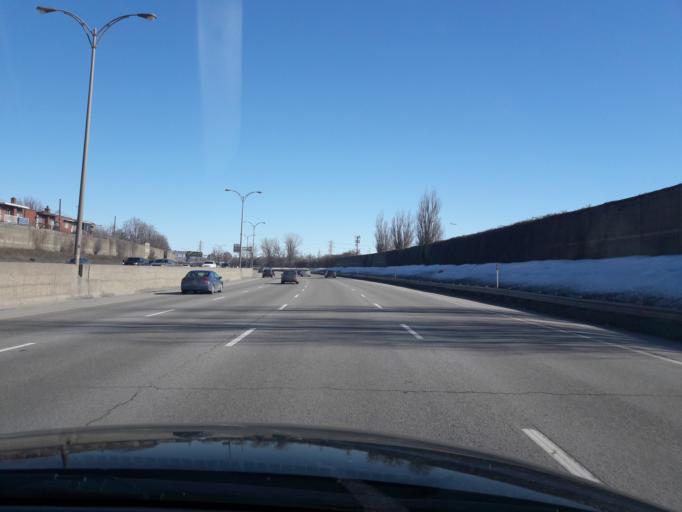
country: CA
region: Quebec
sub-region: Laval
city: Laval
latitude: 45.5319
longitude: -73.6953
